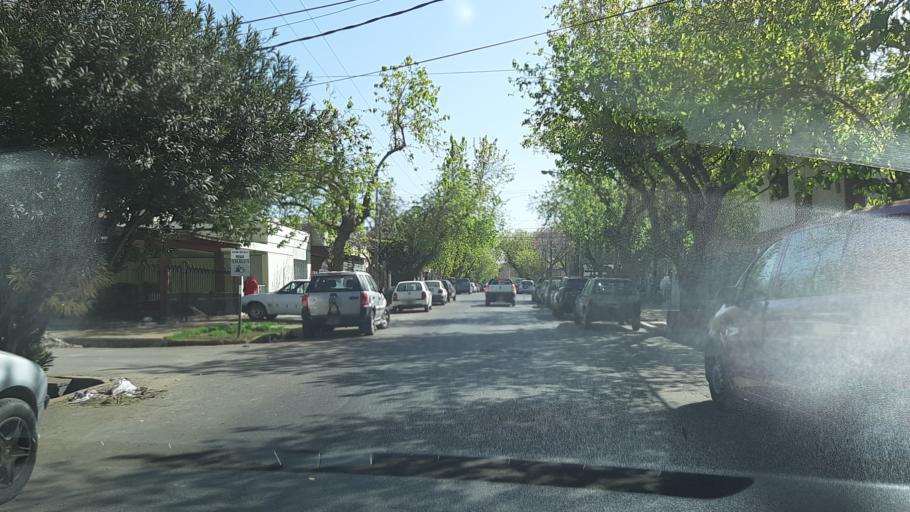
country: AR
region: San Juan
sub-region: Departamento de Santa Lucia
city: Santa Lucia
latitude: -31.5376
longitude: -68.5118
